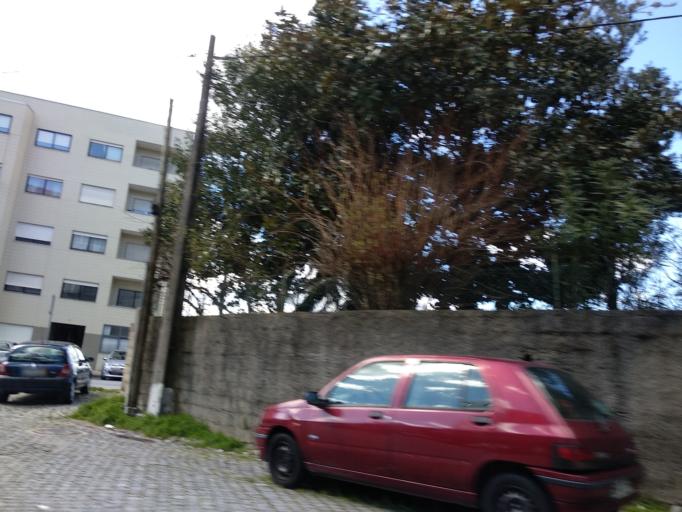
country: PT
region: Braga
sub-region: Braga
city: Braga
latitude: 41.5576
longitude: -8.4032
